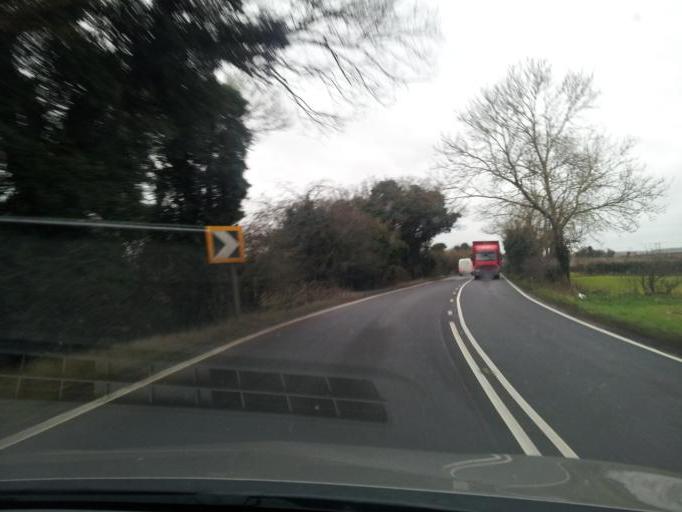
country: GB
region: England
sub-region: Suffolk
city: Ixworth
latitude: 52.3137
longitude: 0.8646
